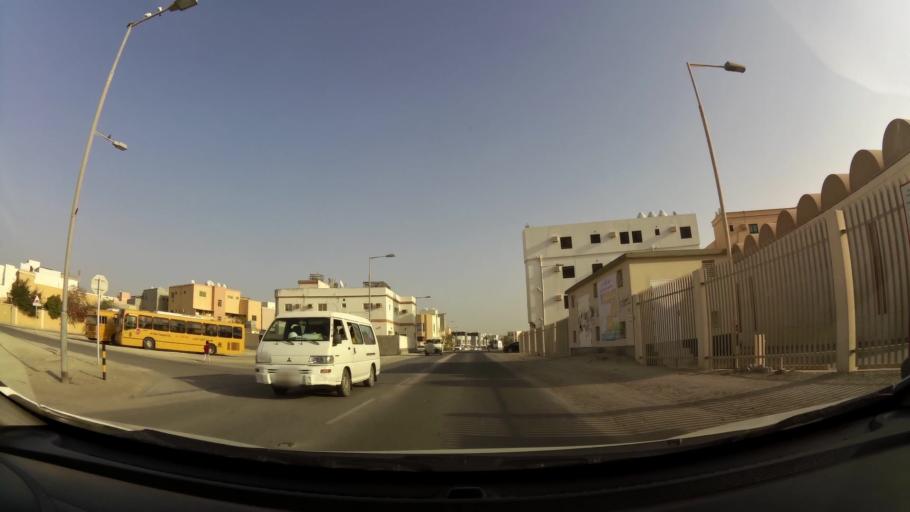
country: BH
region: Manama
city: Jidd Hafs
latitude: 26.2117
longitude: 50.5013
